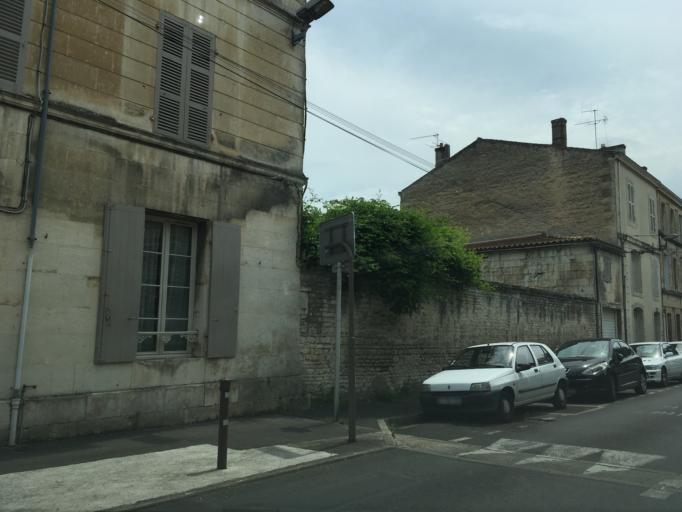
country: FR
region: Poitou-Charentes
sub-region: Departement des Deux-Sevres
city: Niort
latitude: 46.3210
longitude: -0.4677
